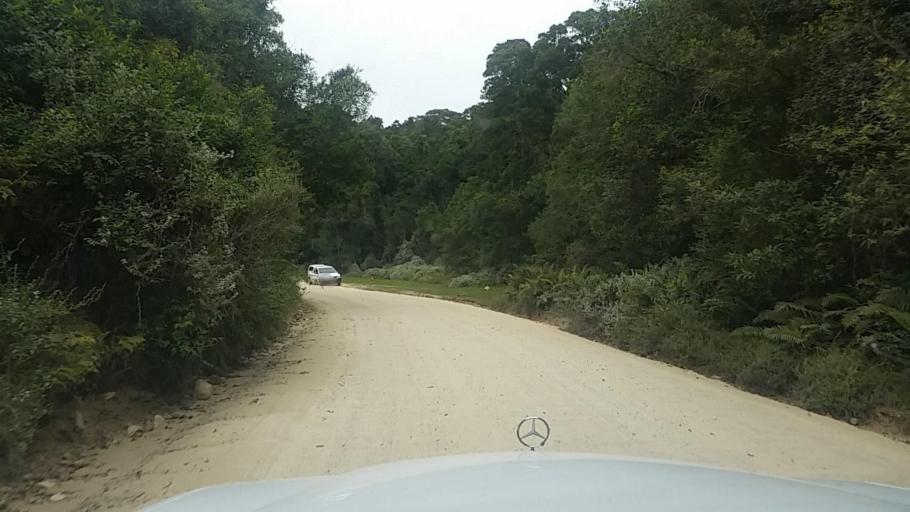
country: ZA
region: Western Cape
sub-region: Eden District Municipality
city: Knysna
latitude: -33.9710
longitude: 23.1458
